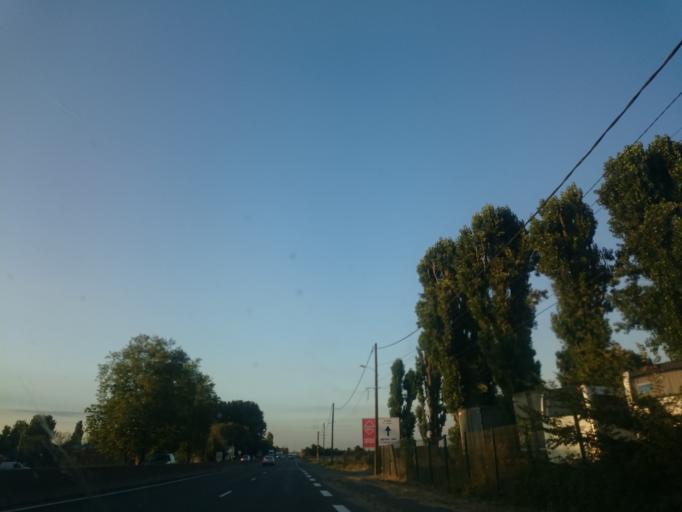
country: FR
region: Ile-de-France
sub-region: Departement de l'Essonne
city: Boissy-sous-Saint-Yon
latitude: 48.5506
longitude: 2.2186
